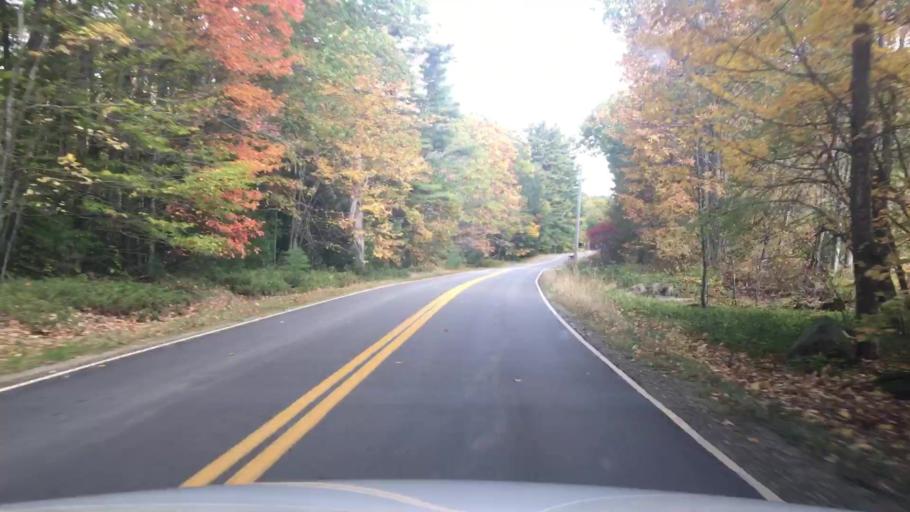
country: US
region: Maine
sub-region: Waldo County
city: Searsmont
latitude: 44.4212
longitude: -69.1418
